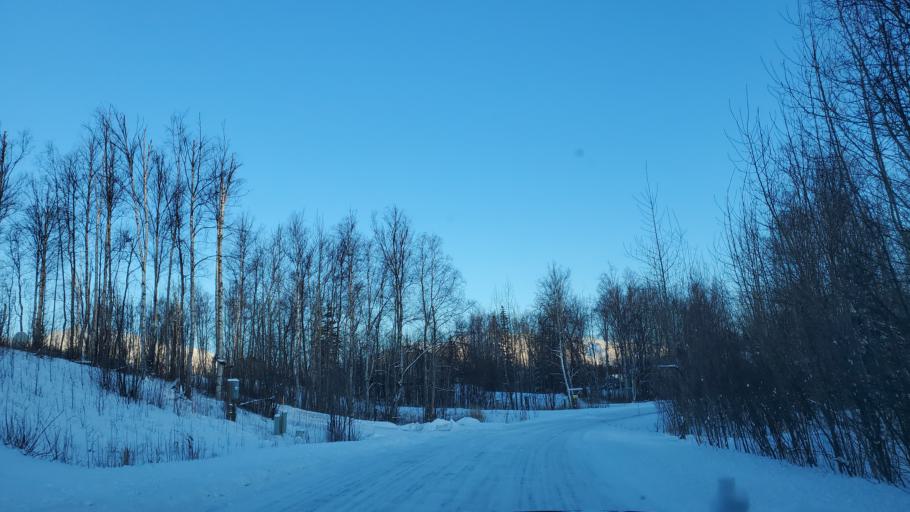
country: US
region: Alaska
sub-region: Matanuska-Susitna Borough
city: Lakes
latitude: 61.6373
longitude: -149.2934
